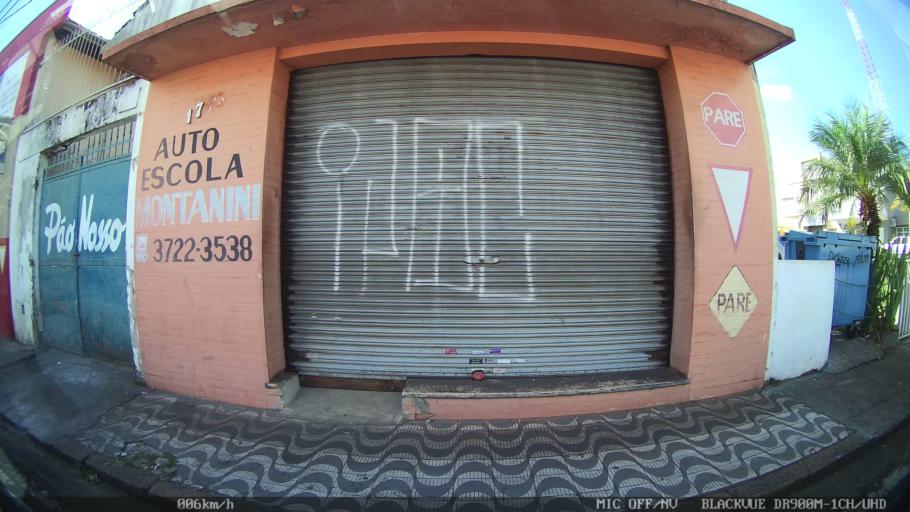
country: BR
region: Sao Paulo
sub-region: Franca
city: Franca
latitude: -20.5355
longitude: -47.3977
